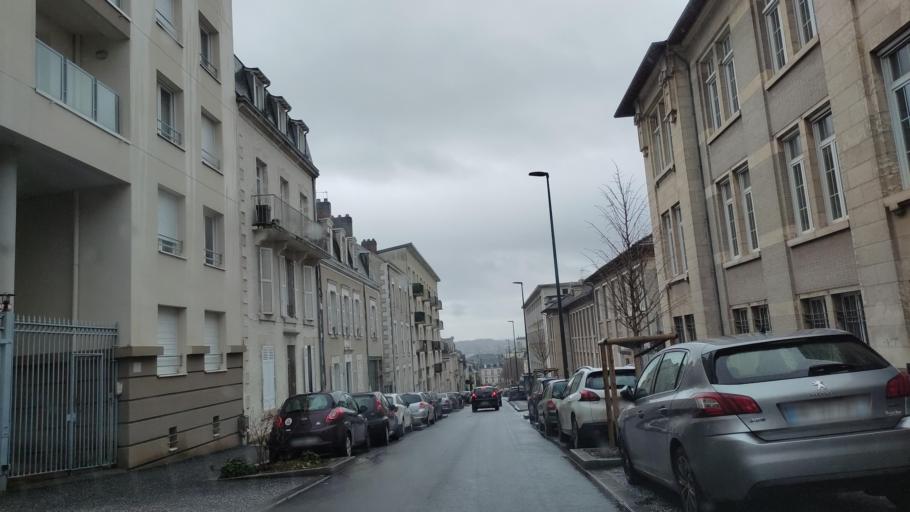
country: FR
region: Limousin
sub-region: Departement de la Haute-Vienne
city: Limoges
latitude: 45.8292
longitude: 1.2494
